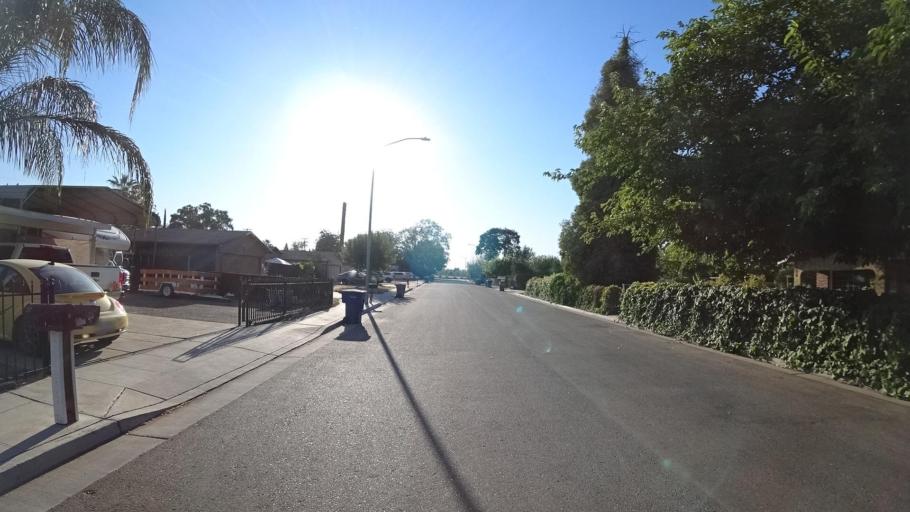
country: US
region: California
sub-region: Fresno County
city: Sunnyside
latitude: 36.7369
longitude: -119.7272
